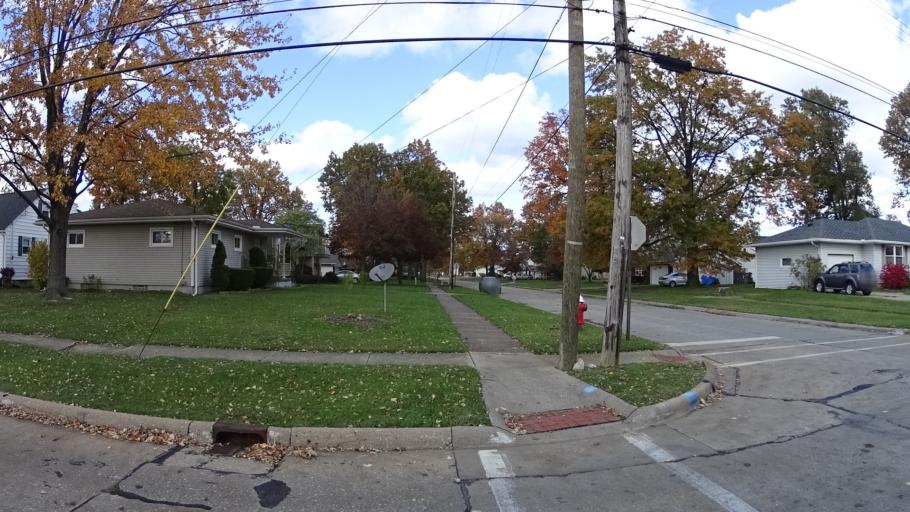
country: US
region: Ohio
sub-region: Lorain County
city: Lorain
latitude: 41.4360
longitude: -82.1934
